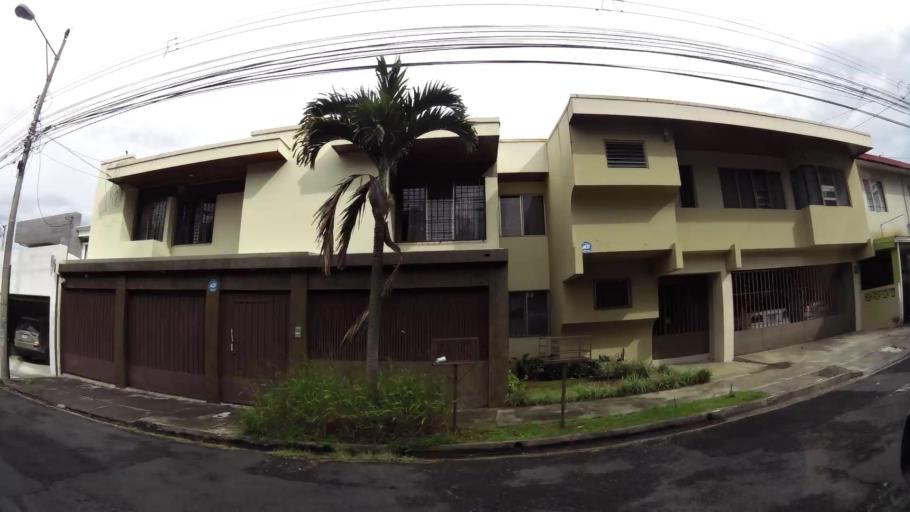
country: CR
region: San Jose
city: San Vicente de Moravia
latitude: 9.9583
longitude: -84.0574
